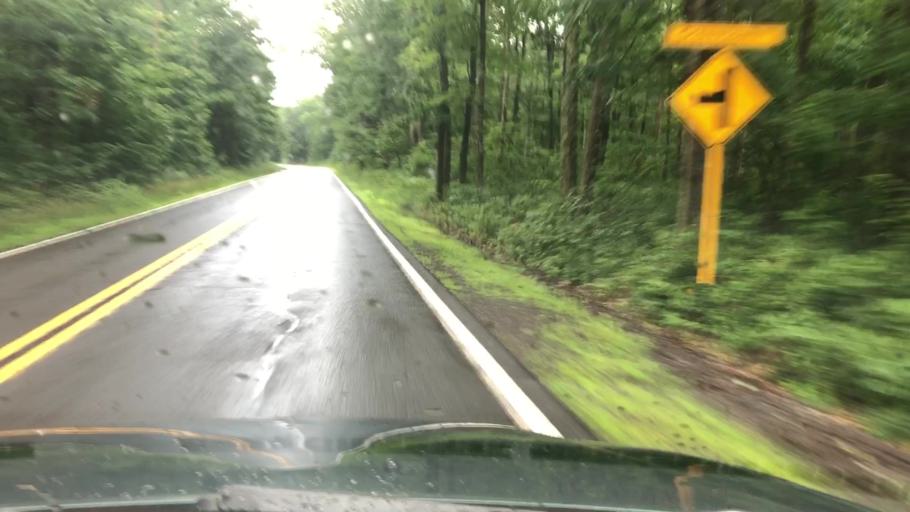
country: US
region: Pennsylvania
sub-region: Wayne County
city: Hawley
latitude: 41.3566
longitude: -75.2059
